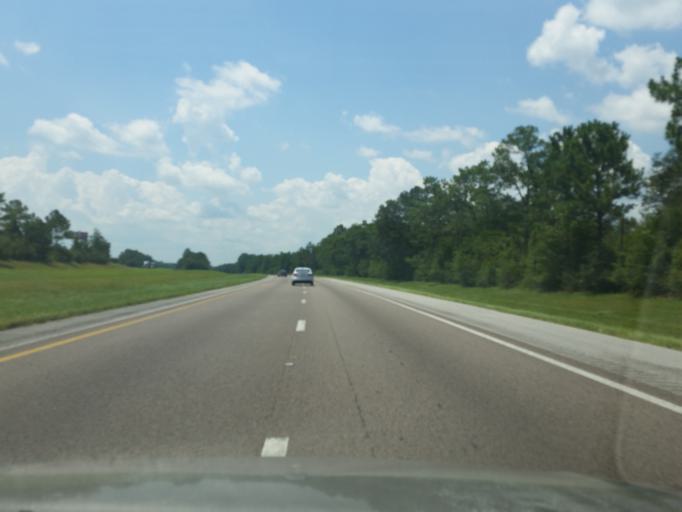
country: US
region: Alabama
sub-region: Baldwin County
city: Robertsdale
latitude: 30.6147
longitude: -87.5735
